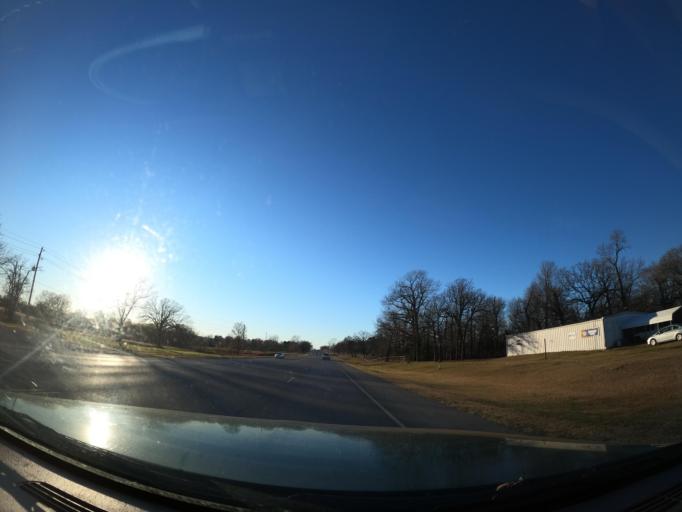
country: US
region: Oklahoma
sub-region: Pittsburg County
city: Krebs
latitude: 34.8940
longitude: -95.6401
